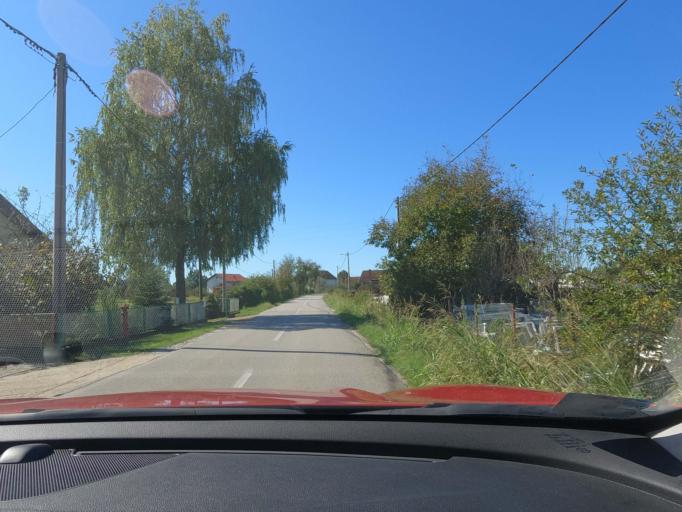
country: HR
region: Sisacko-Moslavacka
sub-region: Grad Sisak
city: Sisak
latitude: 45.4913
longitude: 16.3409
